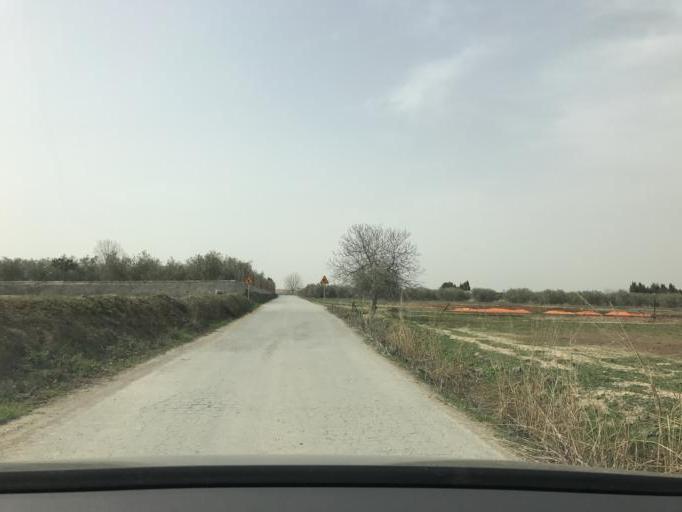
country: ES
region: Andalusia
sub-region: Provincia de Granada
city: Las Gabias
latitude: 37.1682
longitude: -3.7042
